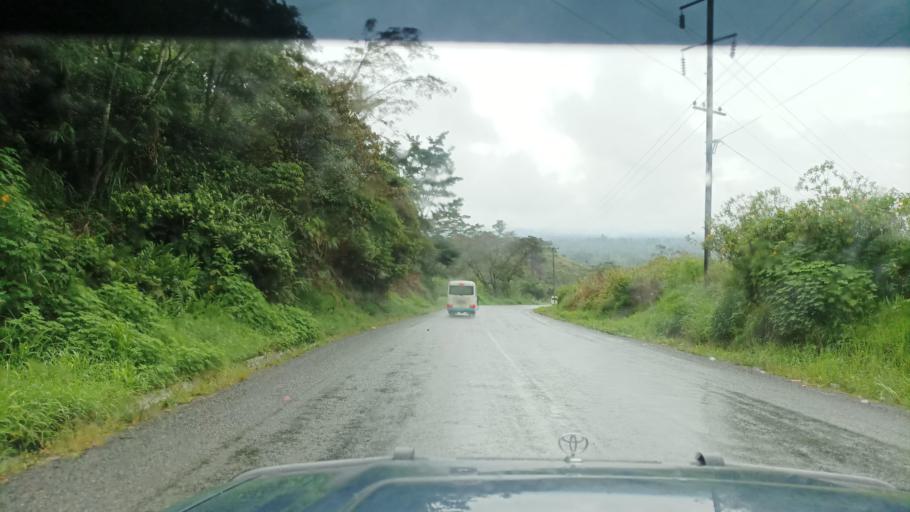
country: PG
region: Western Highlands
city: Rauna
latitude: -5.8265
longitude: 144.3737
